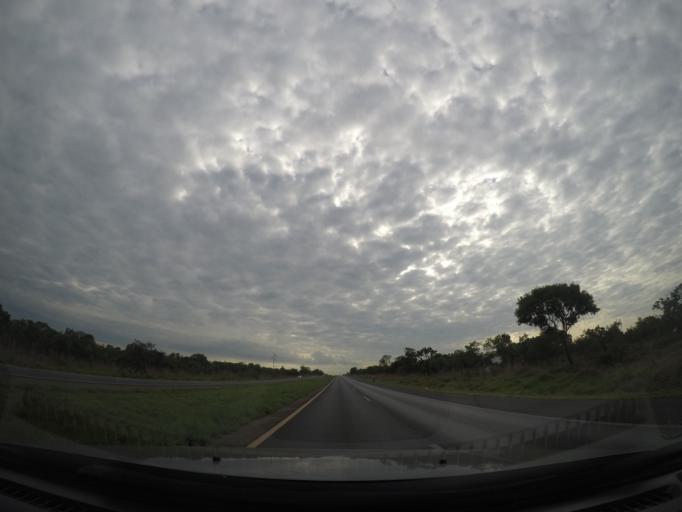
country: BR
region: Goias
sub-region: Planaltina
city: Planaltina
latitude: -15.5961
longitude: -47.6435
